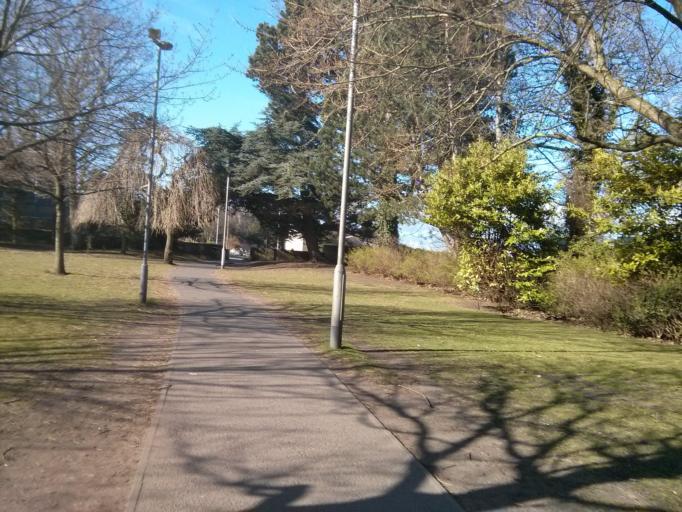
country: GB
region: Scotland
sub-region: Fife
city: Saint Andrews
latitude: 56.3397
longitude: -2.8058
